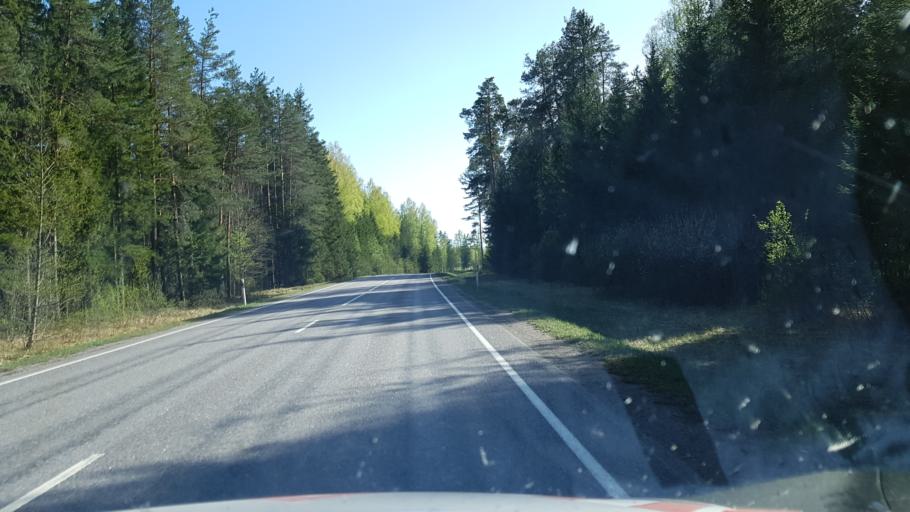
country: EE
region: Paernumaa
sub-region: Saarde vald
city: Kilingi-Nomme
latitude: 58.1858
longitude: 25.0541
